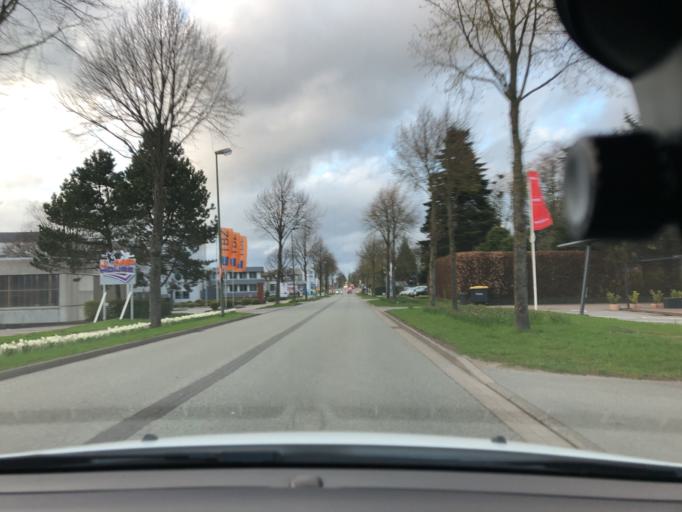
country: DE
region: Schleswig-Holstein
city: Flensburg
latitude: 54.7675
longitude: 9.4352
